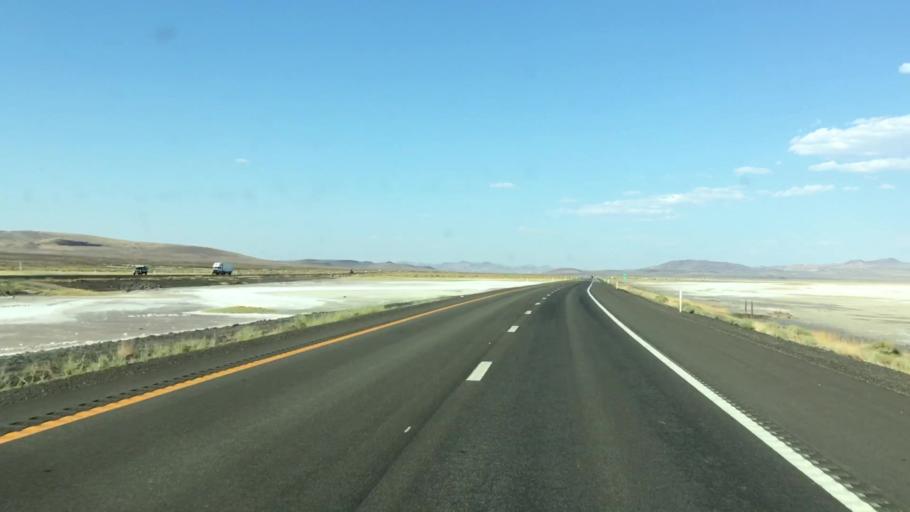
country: US
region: Nevada
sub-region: Lyon County
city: Fernley
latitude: 39.7047
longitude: -119.0957
